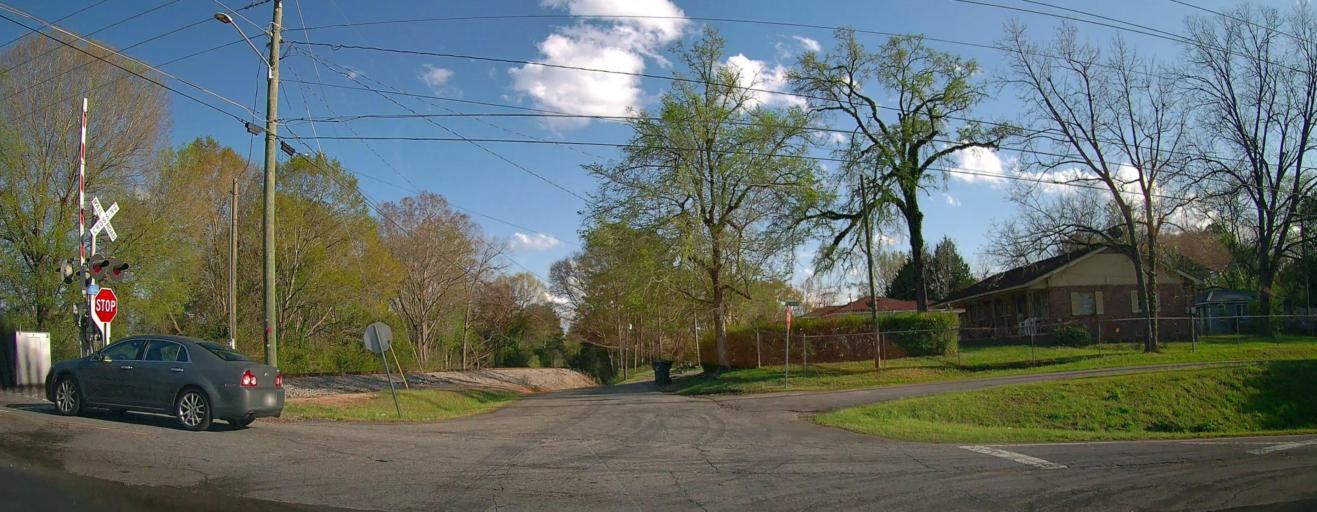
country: US
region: Georgia
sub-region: Baldwin County
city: Milledgeville
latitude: 33.0751
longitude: -83.2360
